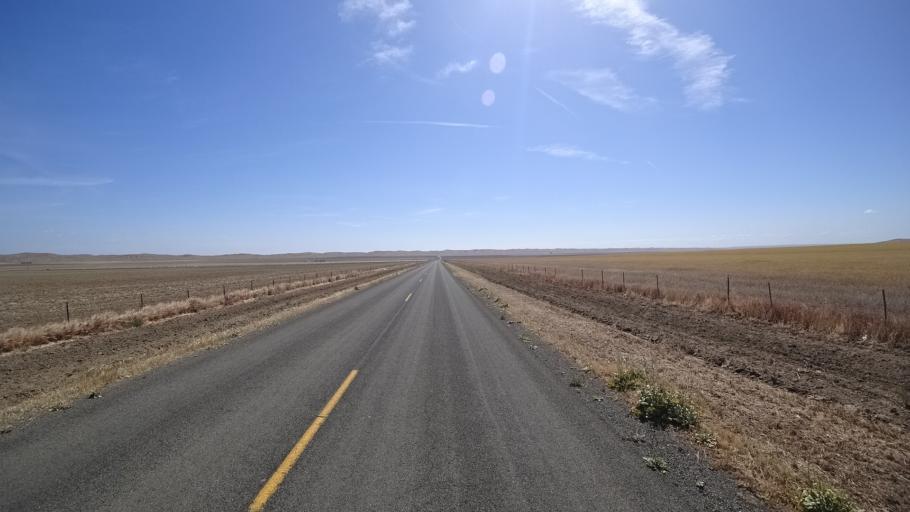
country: US
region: California
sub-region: Kings County
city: Avenal
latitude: 35.9351
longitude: -120.0817
